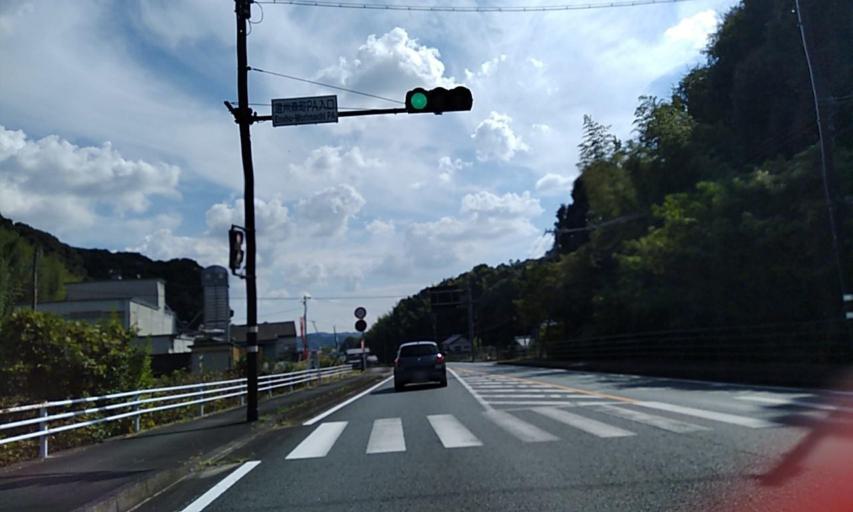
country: JP
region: Shizuoka
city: Mori
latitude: 34.8226
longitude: 137.9038
